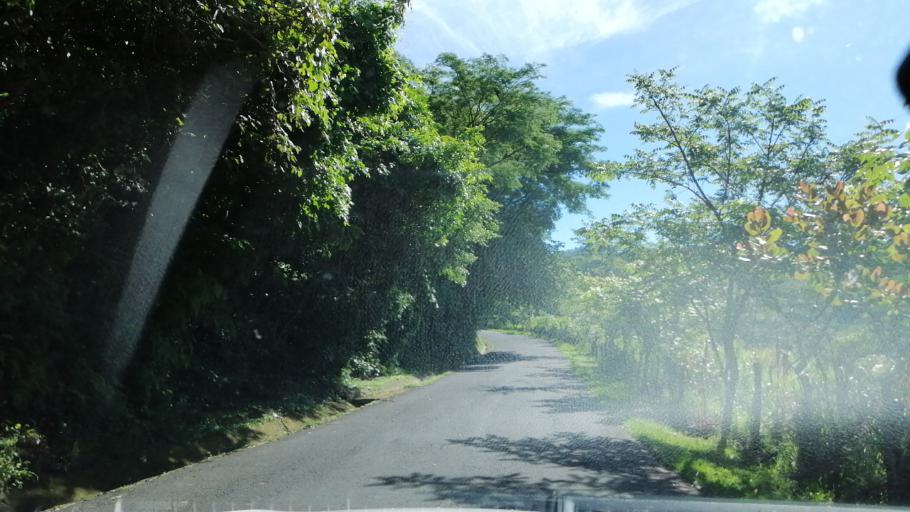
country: SV
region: Morazan
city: Corinto
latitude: 13.8077
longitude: -88.0030
